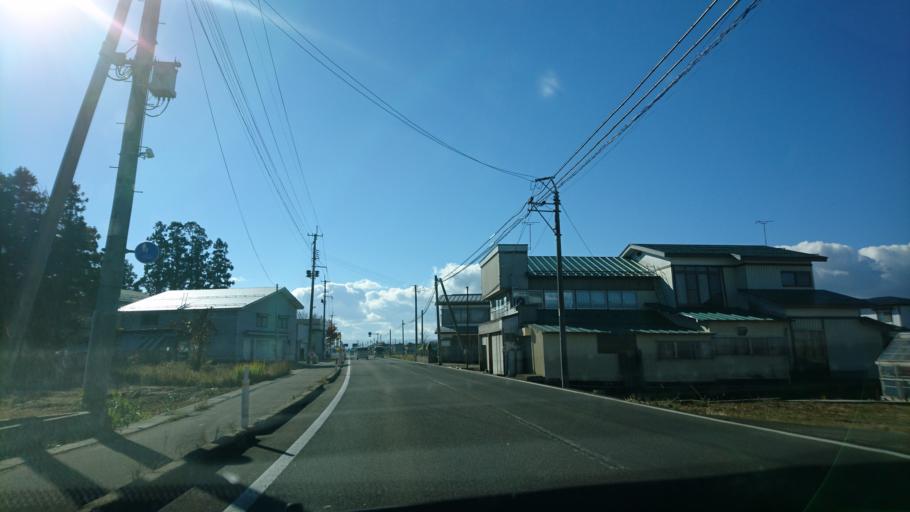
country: JP
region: Akita
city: Yokotemachi
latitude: 39.2877
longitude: 140.5217
